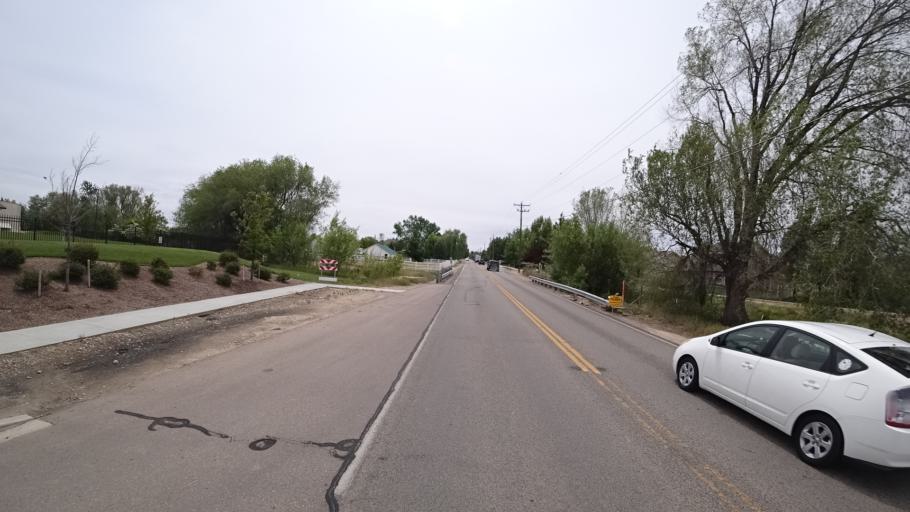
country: US
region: Idaho
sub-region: Ada County
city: Meridian
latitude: 43.5735
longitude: -116.3746
